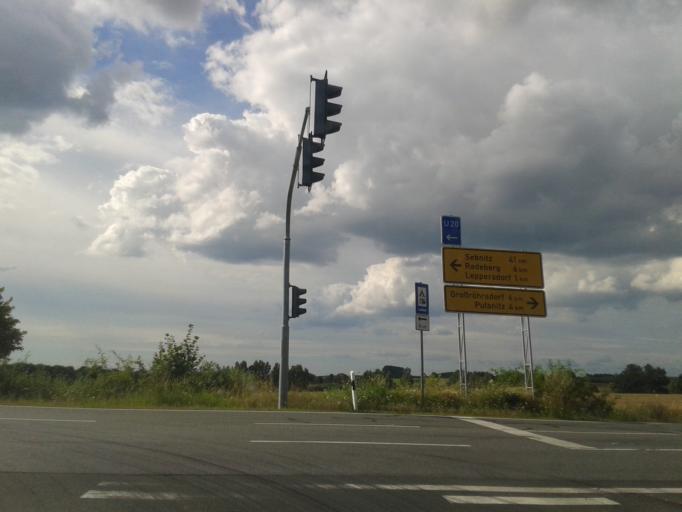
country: DE
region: Saxony
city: Lichtenberg
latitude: 51.1593
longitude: 13.9756
